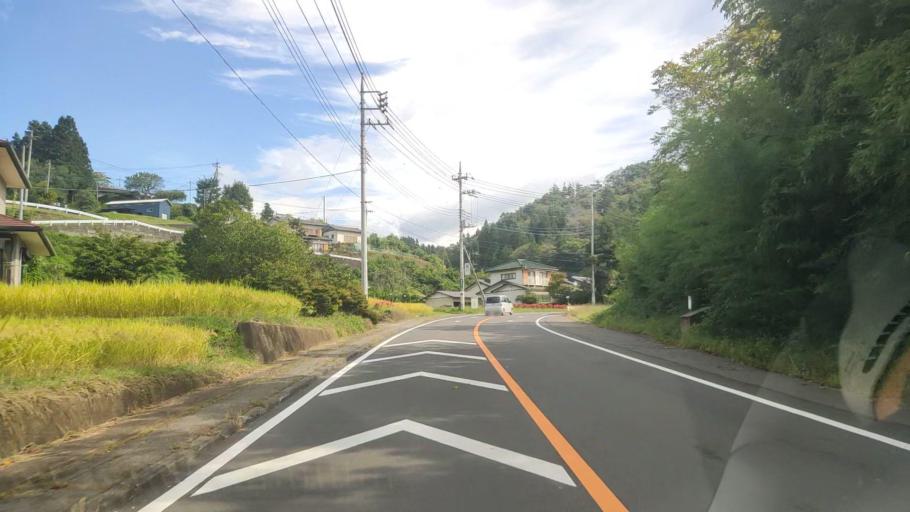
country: JP
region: Gunma
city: Nakanojomachi
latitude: 36.6203
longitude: 138.9054
